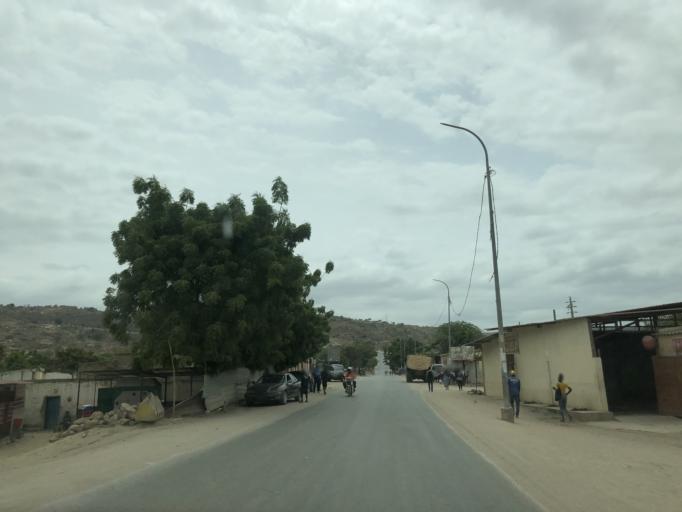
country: AO
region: Cuanza Sul
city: Sumbe
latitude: -11.1816
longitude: 13.8653
